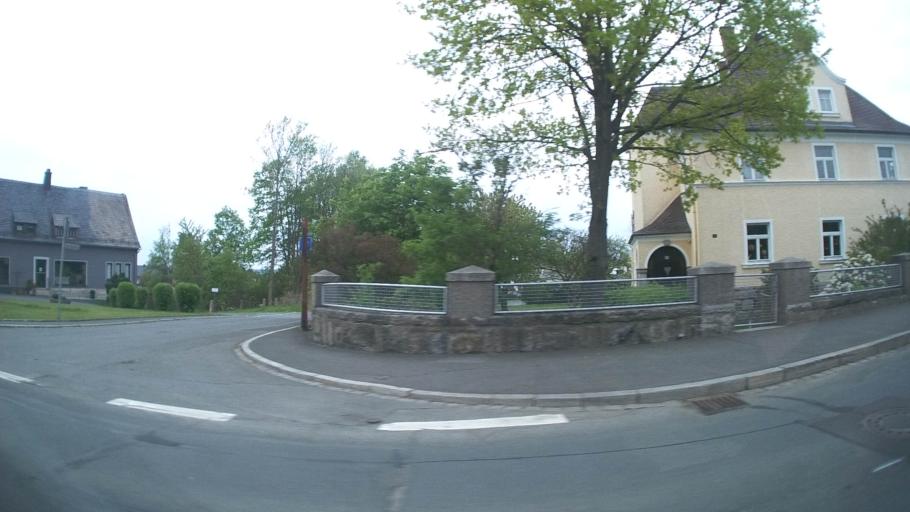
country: DE
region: Bavaria
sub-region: Upper Franconia
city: Sparneck
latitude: 50.1621
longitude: 11.8389
